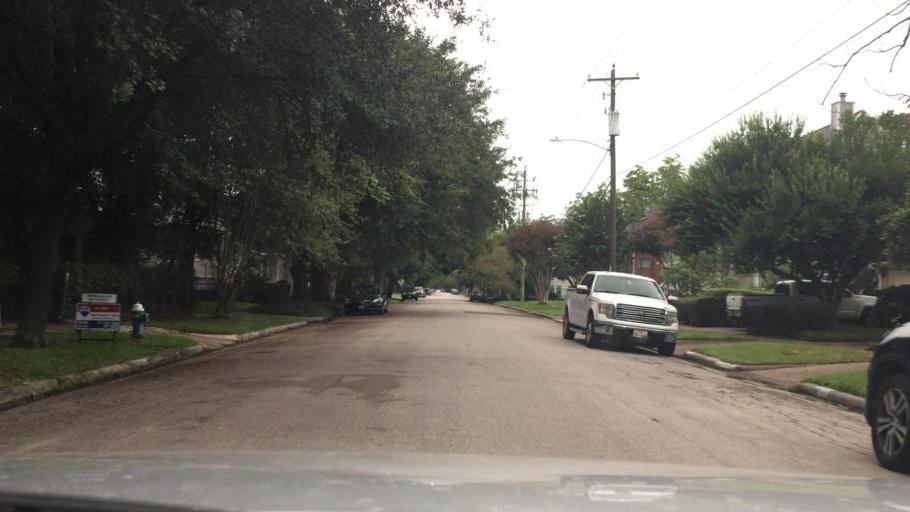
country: US
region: Texas
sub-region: Harris County
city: Houston
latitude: 29.7926
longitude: -95.3907
